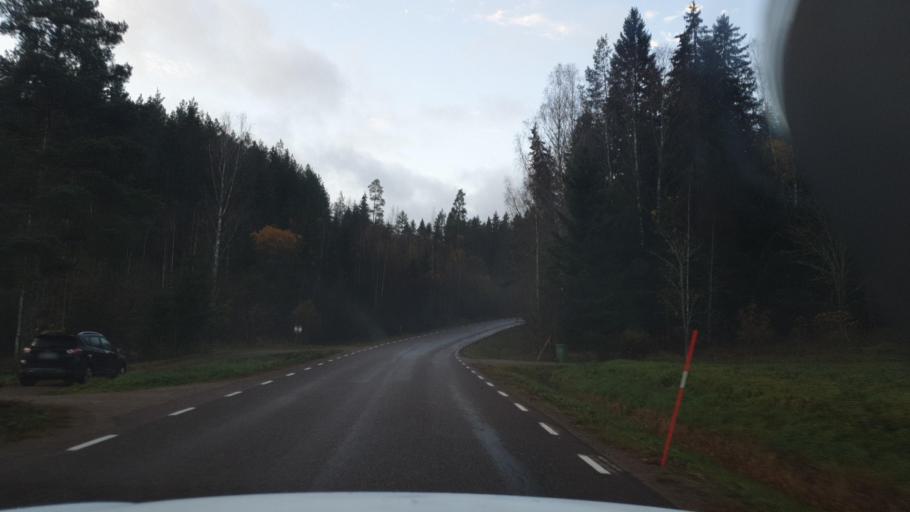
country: SE
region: Vaermland
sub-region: Arvika Kommun
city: Arvika
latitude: 59.6168
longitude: 12.7865
